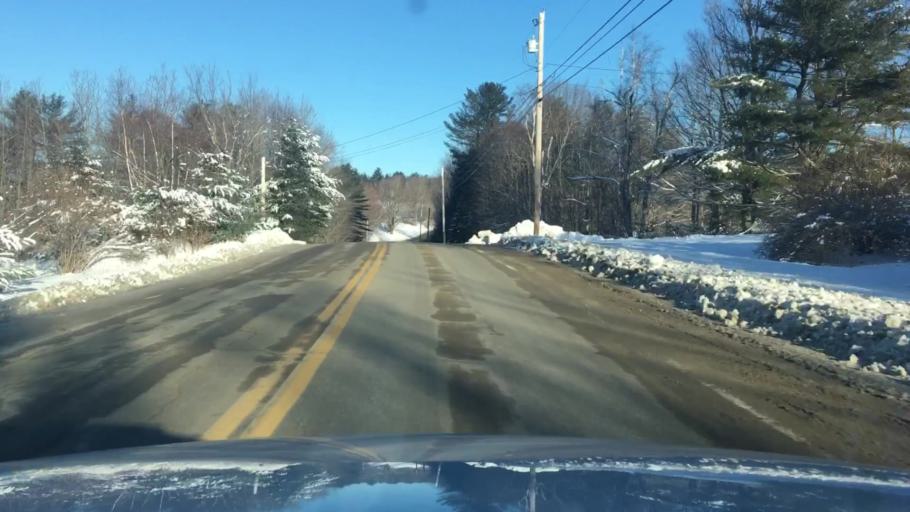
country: US
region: Maine
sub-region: Kennebec County
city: Mount Vernon
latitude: 44.4462
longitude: -69.9687
